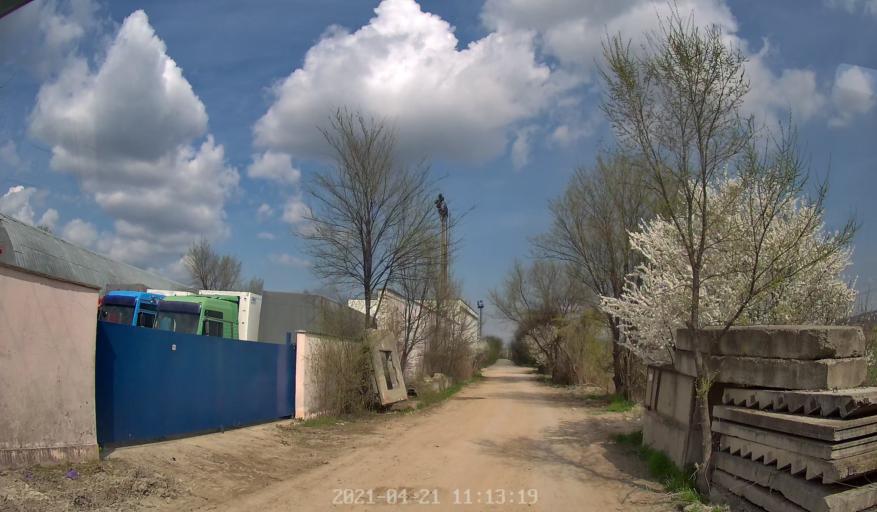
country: MD
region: Chisinau
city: Singera
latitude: 46.9557
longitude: 28.9317
